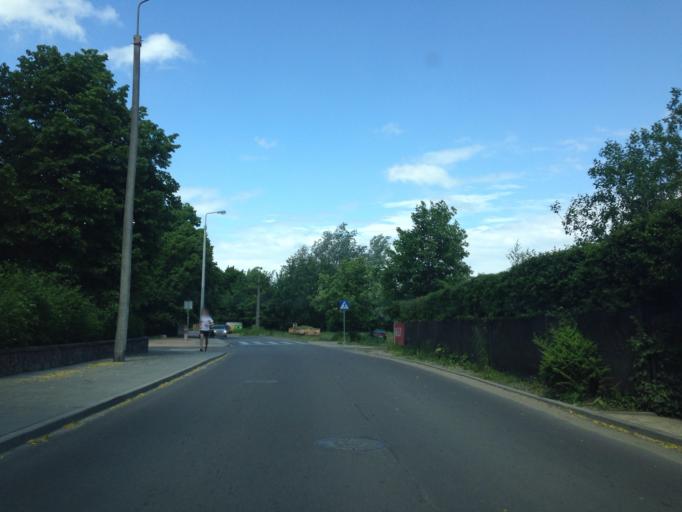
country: PL
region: Pomeranian Voivodeship
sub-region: Gdansk
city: Gdansk
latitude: 54.3273
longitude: 18.6323
